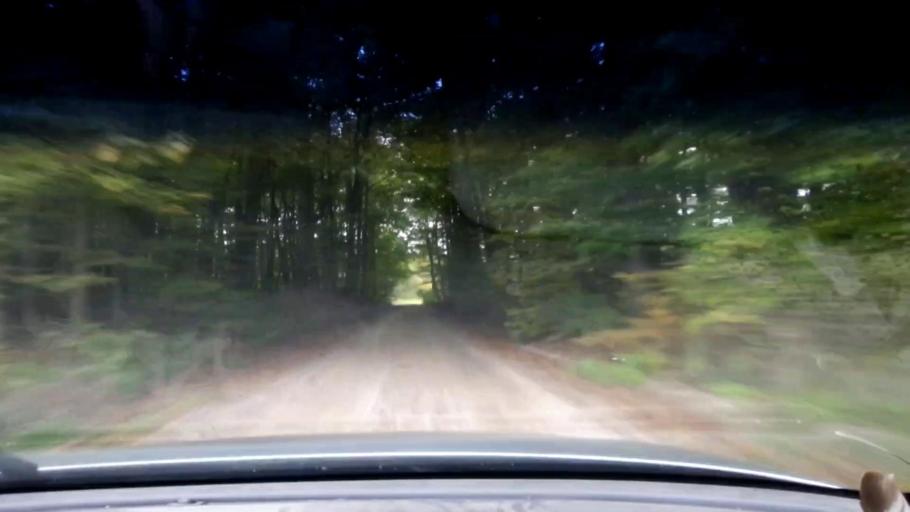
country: DE
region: Bavaria
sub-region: Upper Franconia
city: Burgwindheim
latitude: 49.8326
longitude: 10.6471
